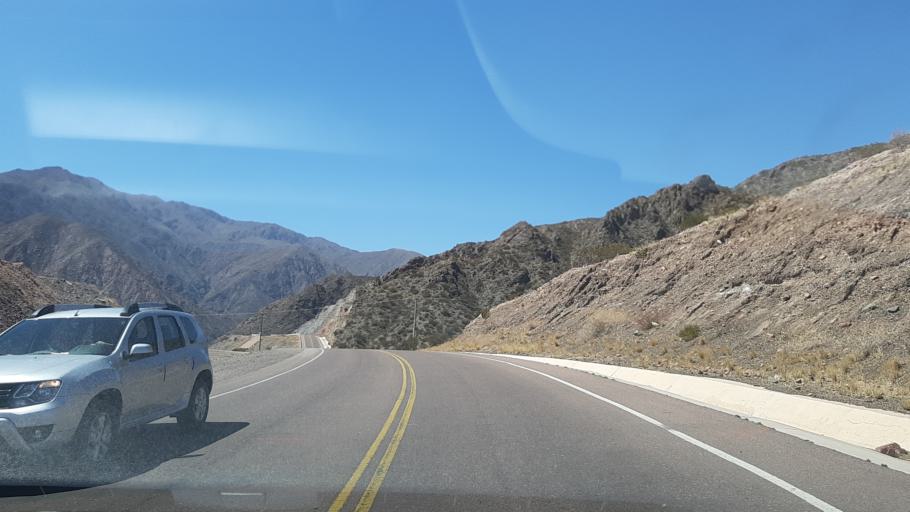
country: AR
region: Mendoza
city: Lujan de Cuyo
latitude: -32.9925
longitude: -69.1623
